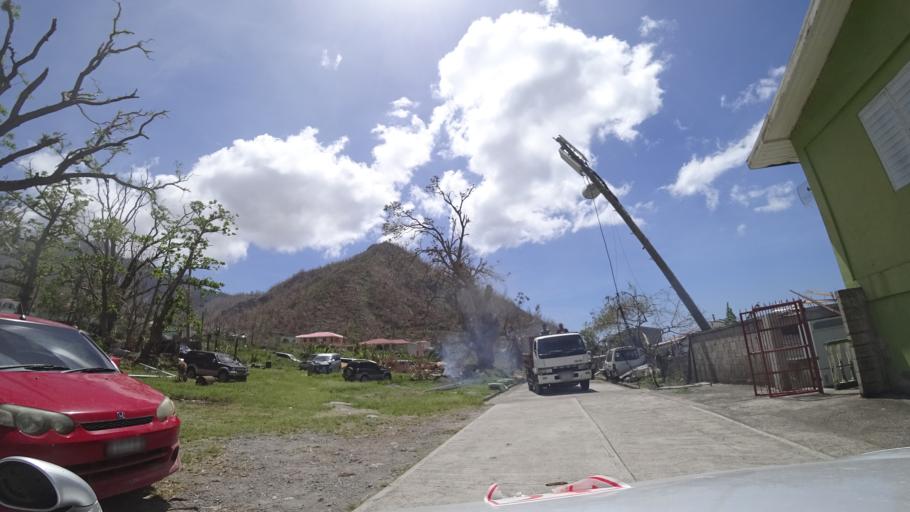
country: DM
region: Saint Luke
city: Pointe Michel
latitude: 15.2614
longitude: -61.3754
